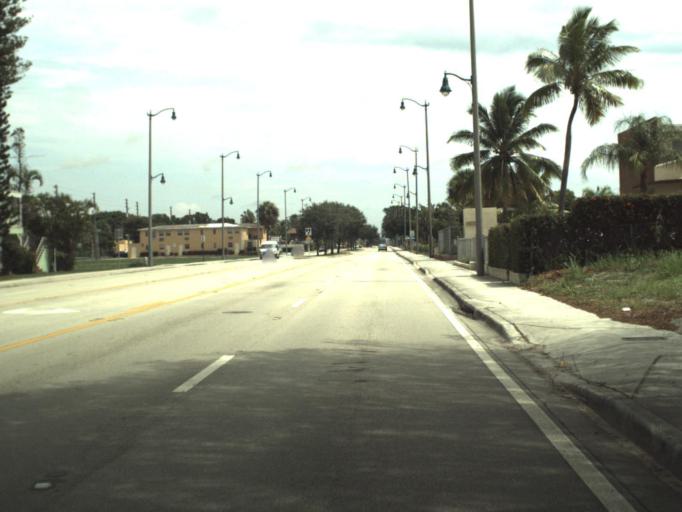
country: US
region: Florida
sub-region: Palm Beach County
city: West Palm Beach
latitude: 26.7401
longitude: -80.0566
